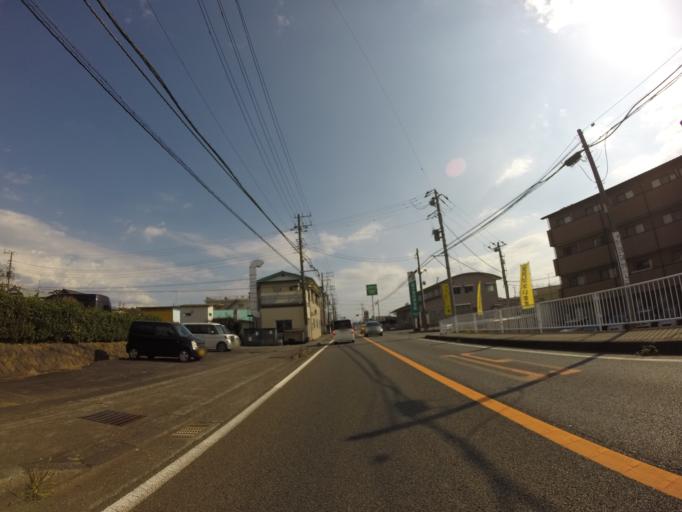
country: JP
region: Shizuoka
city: Fujinomiya
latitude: 35.2129
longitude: 138.6334
